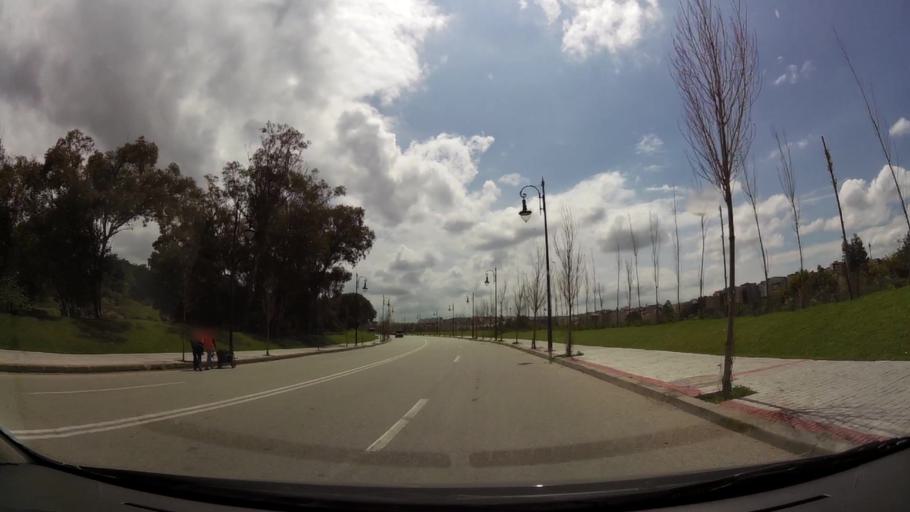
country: MA
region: Tanger-Tetouan
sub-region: Tanger-Assilah
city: Tangier
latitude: 35.7750
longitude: -5.7621
